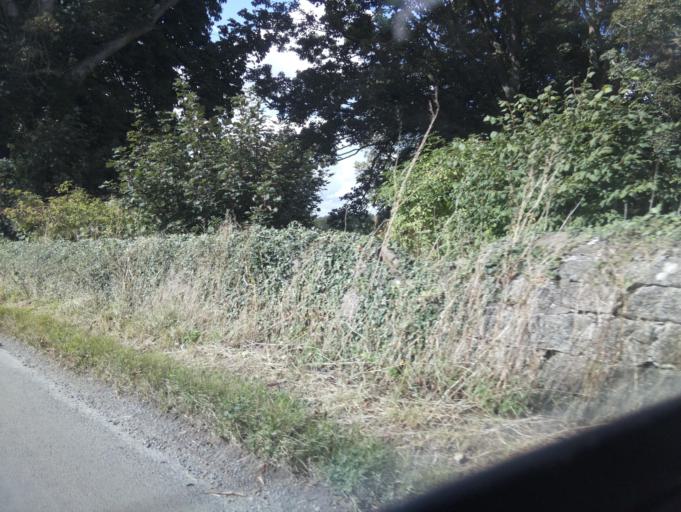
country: GB
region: England
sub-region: North Yorkshire
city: Leyburn
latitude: 54.2624
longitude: -1.7272
